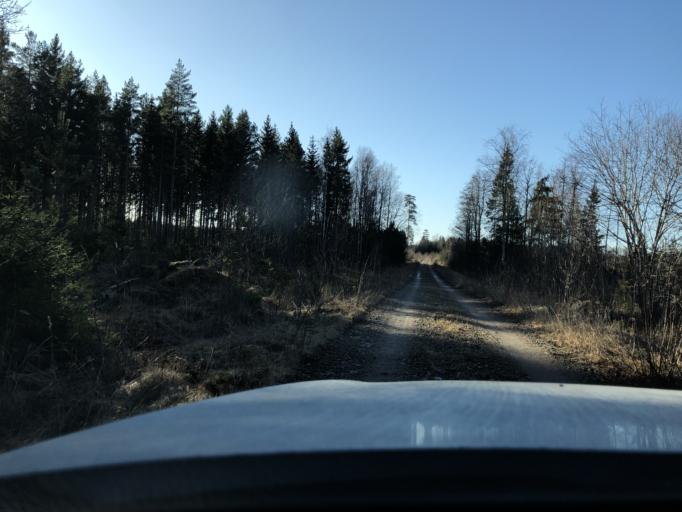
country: SE
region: Gaevleborg
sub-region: Gavle Kommun
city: Hedesunda
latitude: 60.3016
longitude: 16.8922
